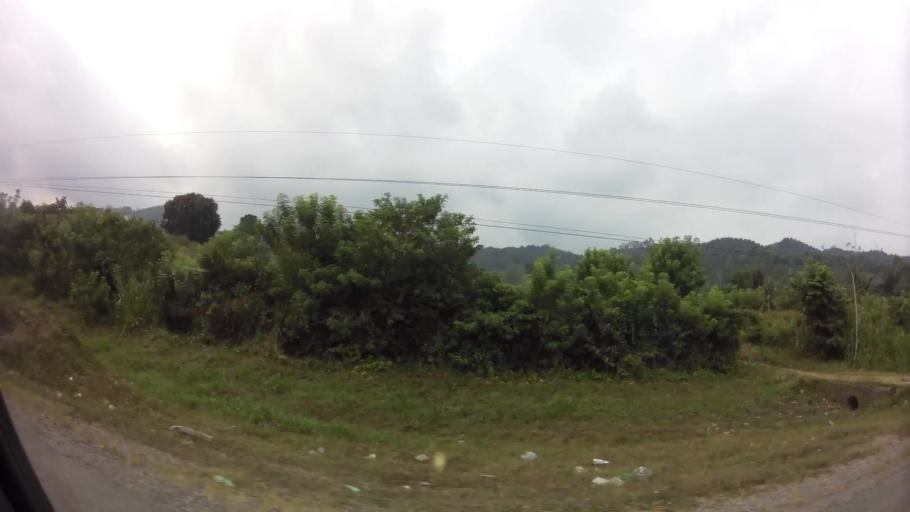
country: HN
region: Yoro
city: Guaimitas
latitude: 15.4946
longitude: -87.7294
